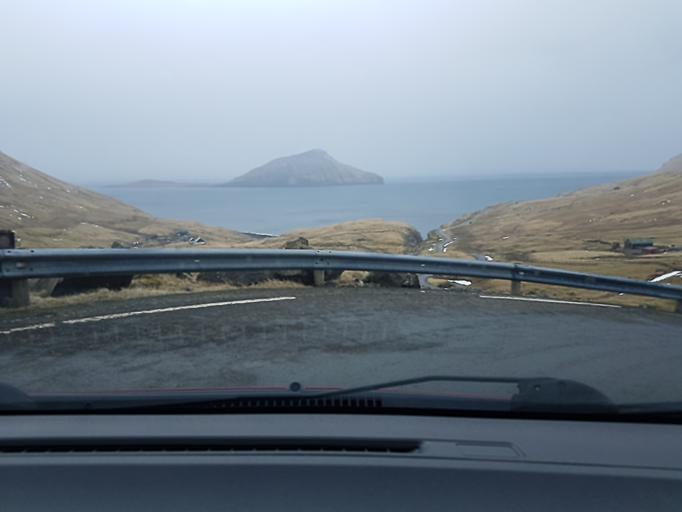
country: FO
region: Streymoy
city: Kollafjordhur
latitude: 62.0467
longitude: -6.9221
